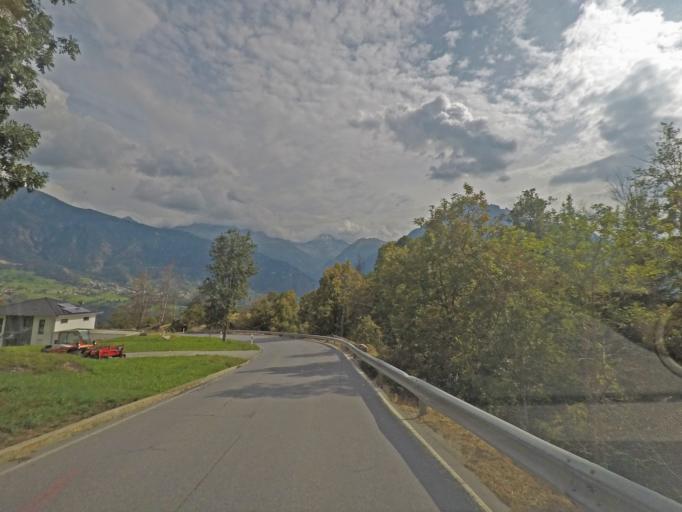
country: CH
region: Valais
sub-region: Brig District
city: Naters
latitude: 46.3345
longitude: 7.9842
